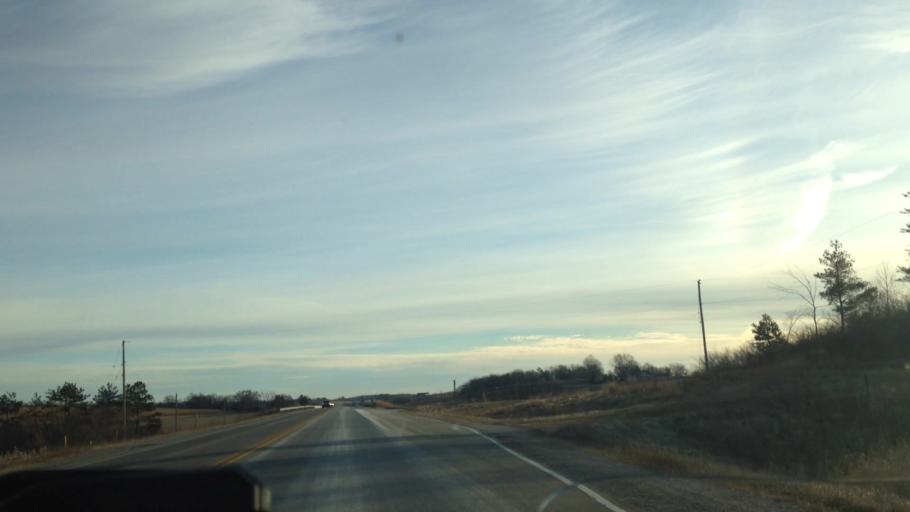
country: US
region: Wisconsin
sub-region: Dodge County
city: Theresa
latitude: 43.5365
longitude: -88.4370
